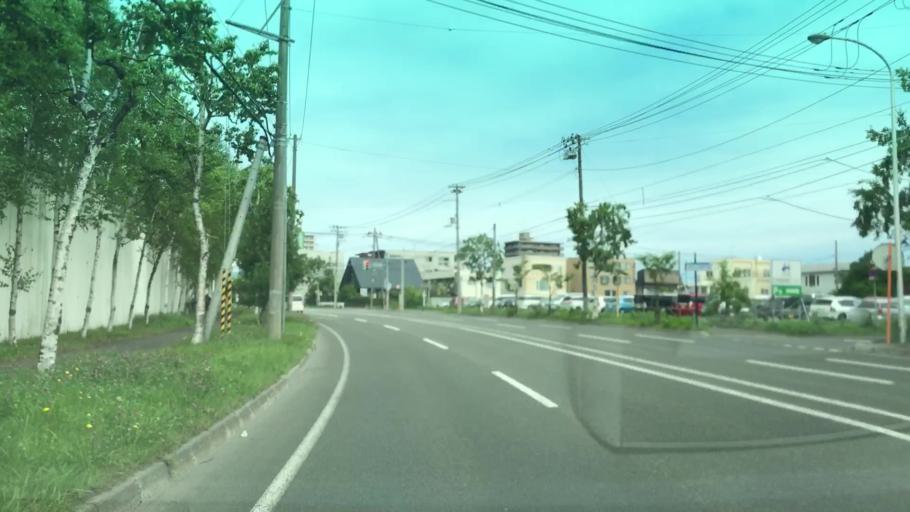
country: JP
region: Hokkaido
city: Sapporo
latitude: 43.0697
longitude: 141.2874
